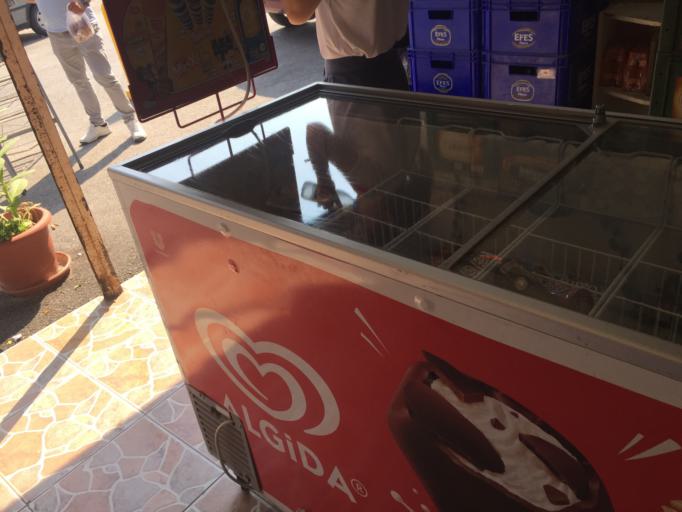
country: TR
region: Izmir
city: Urla
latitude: 38.3238
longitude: 26.7644
